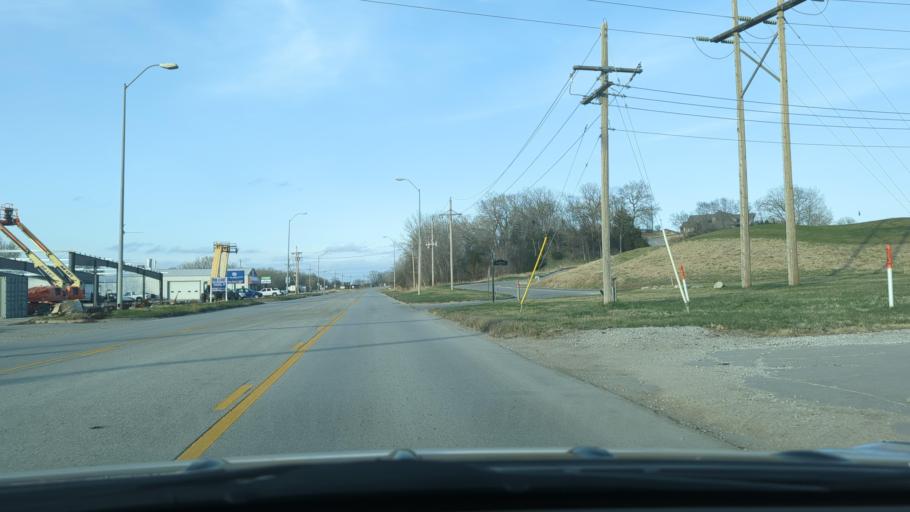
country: US
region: Nebraska
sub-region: Saunders County
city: Ashland
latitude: 41.0409
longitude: -96.3544
